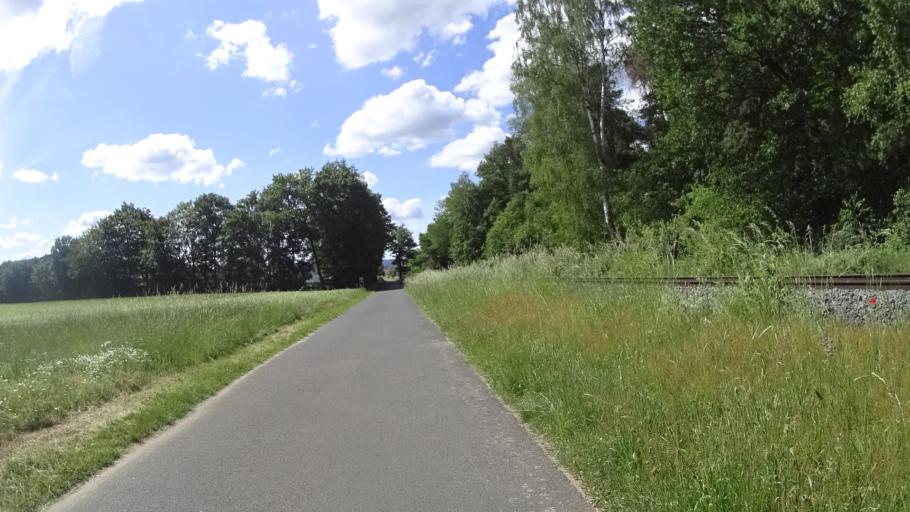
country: DE
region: Bavaria
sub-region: Regierungsbezirk Unterfranken
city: Erlenbach am Main
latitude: 49.8120
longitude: 9.1540
